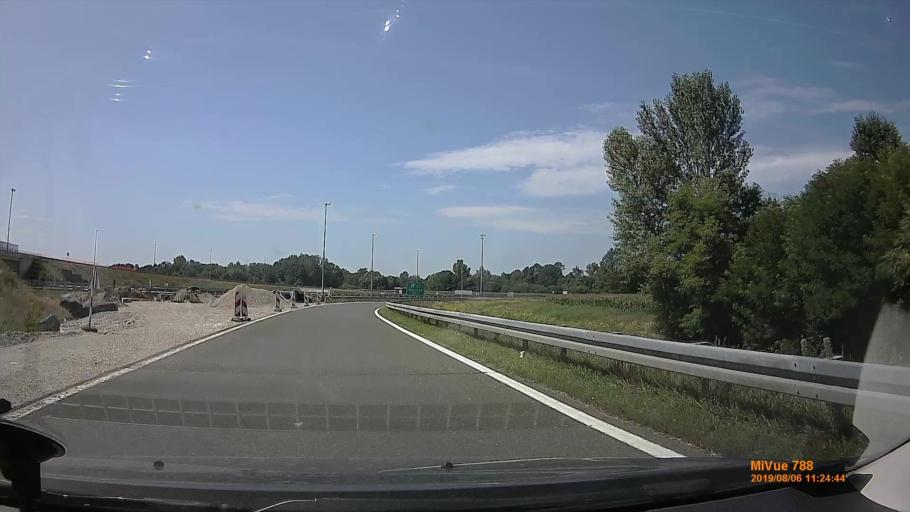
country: HR
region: Medimurska
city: Gorican
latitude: 46.4087
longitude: 16.6856
